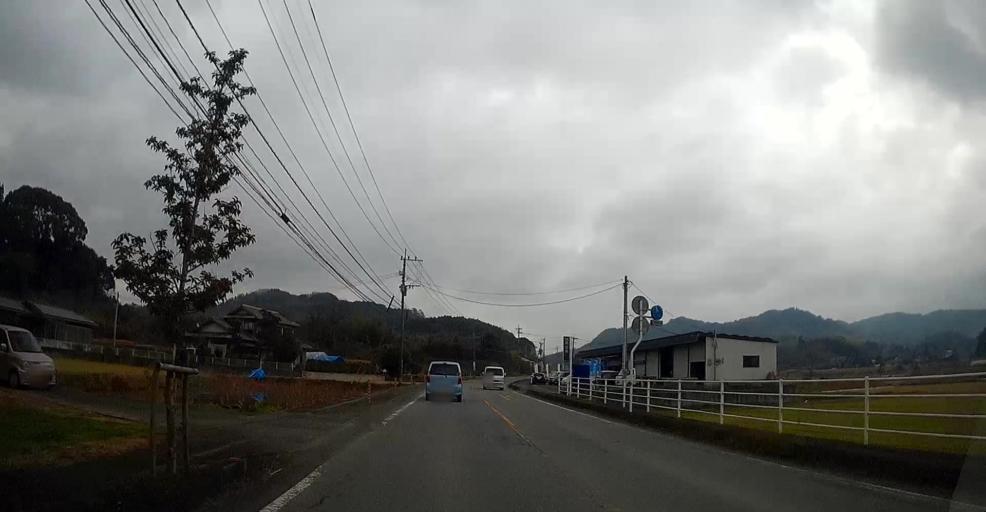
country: JP
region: Kumamoto
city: Matsubase
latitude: 32.6489
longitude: 130.7184
